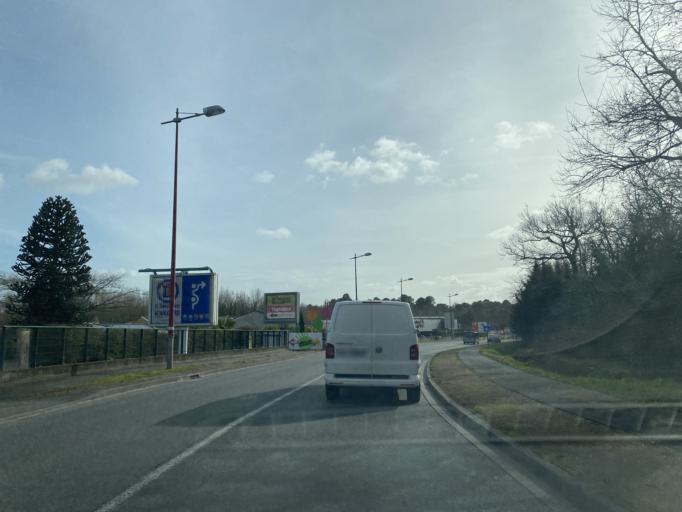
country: FR
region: Aquitaine
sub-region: Departement de la Gironde
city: Le Taillan-Medoc
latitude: 44.9152
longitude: -0.6690
